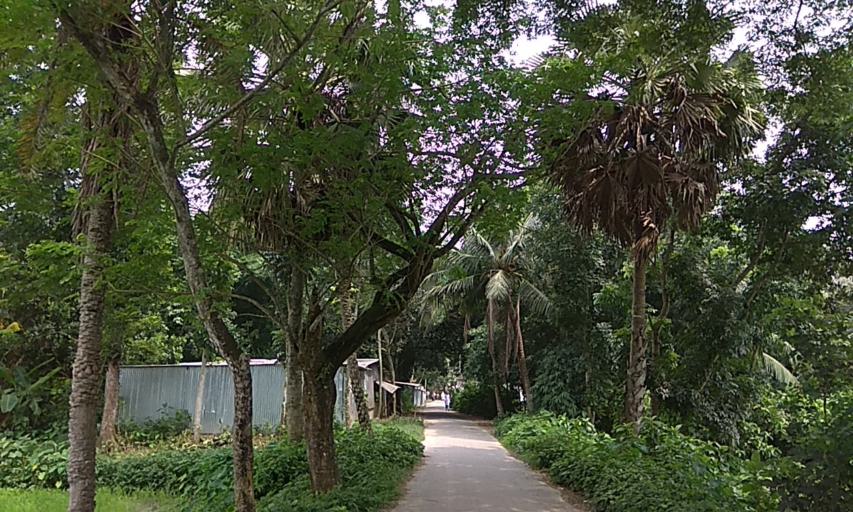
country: BD
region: Dhaka
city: Faridpur
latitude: 23.5340
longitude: 89.9696
